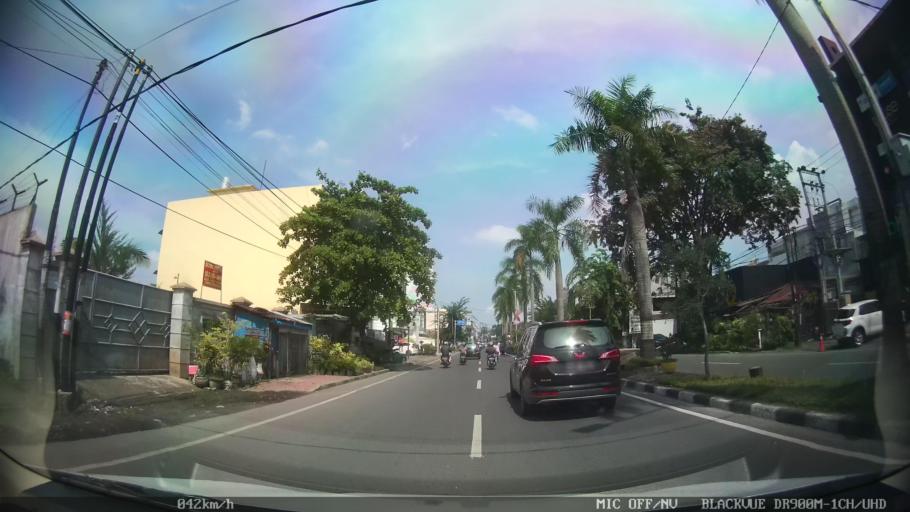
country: ID
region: North Sumatra
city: Medan
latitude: 3.6072
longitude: 98.6669
